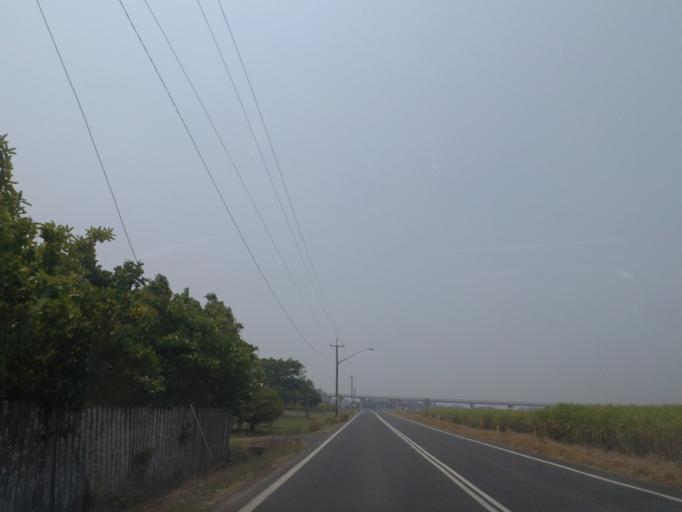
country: AU
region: New South Wales
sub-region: Richmond Valley
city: Evans Head
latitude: -29.0015
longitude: 153.4376
